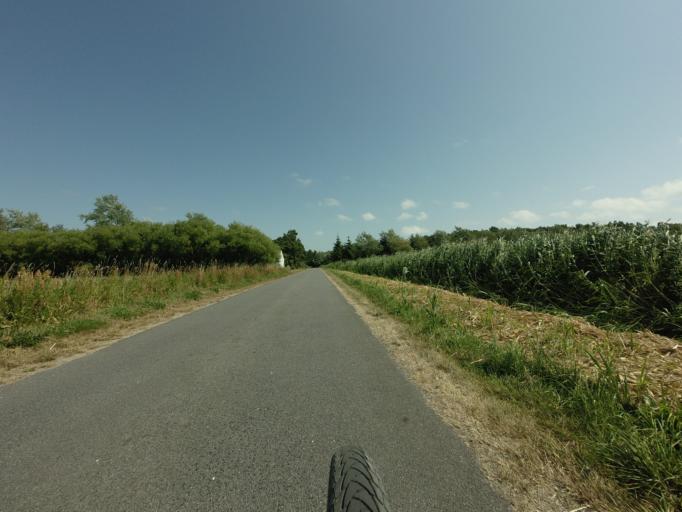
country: DK
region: North Denmark
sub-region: Laeso Kommune
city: Byrum
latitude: 57.2518
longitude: 10.9820
